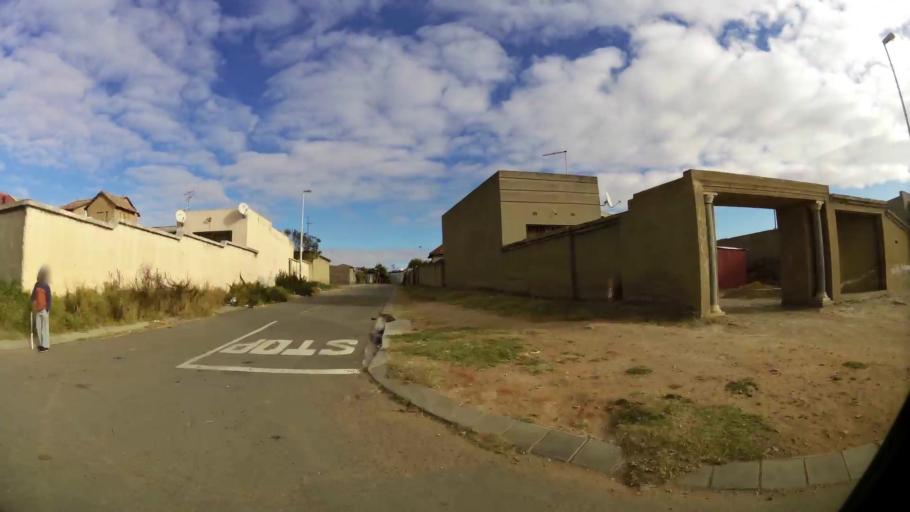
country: ZA
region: Gauteng
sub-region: City of Johannesburg Metropolitan Municipality
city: Modderfontein
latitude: -26.0436
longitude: 28.1869
